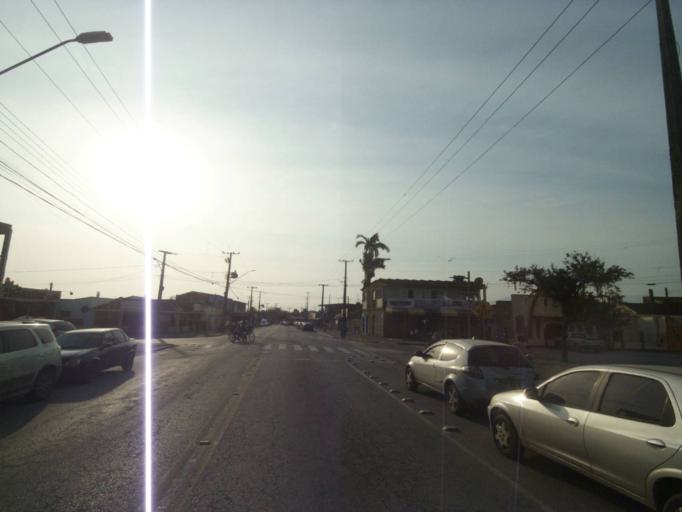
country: BR
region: Parana
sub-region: Paranagua
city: Paranagua
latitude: -25.5180
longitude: -48.5389
